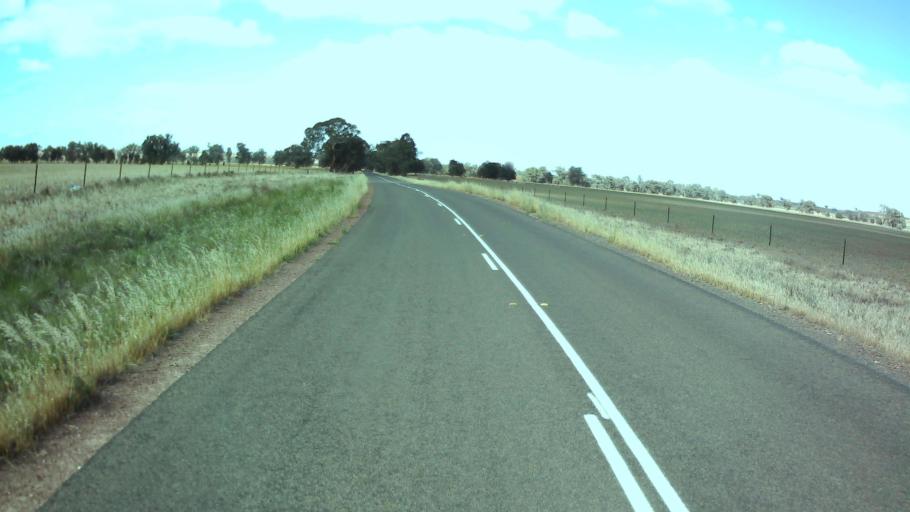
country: AU
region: New South Wales
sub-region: Weddin
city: Grenfell
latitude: -33.9791
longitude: 148.4199
